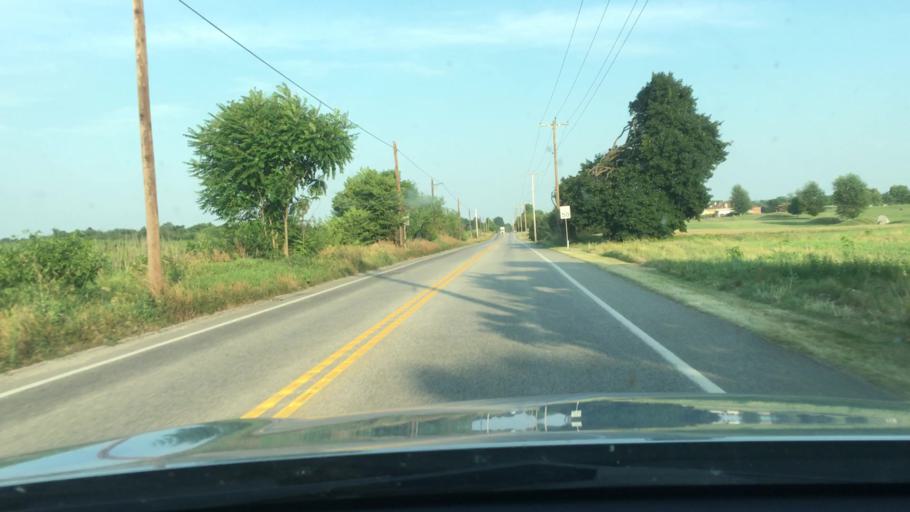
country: US
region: Pennsylvania
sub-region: Cumberland County
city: Boiling Springs
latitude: 40.1859
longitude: -77.1487
